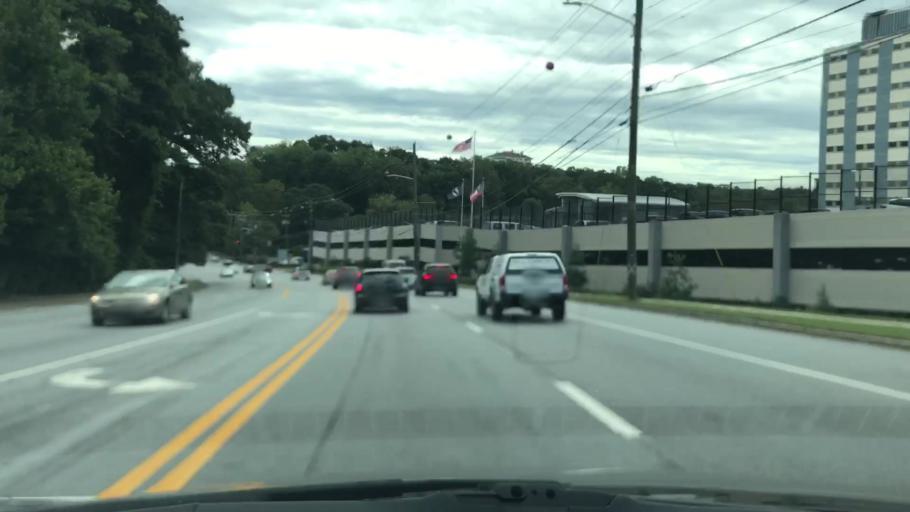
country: US
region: Georgia
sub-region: DeKalb County
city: North Decatur
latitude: 33.8032
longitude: -84.3107
